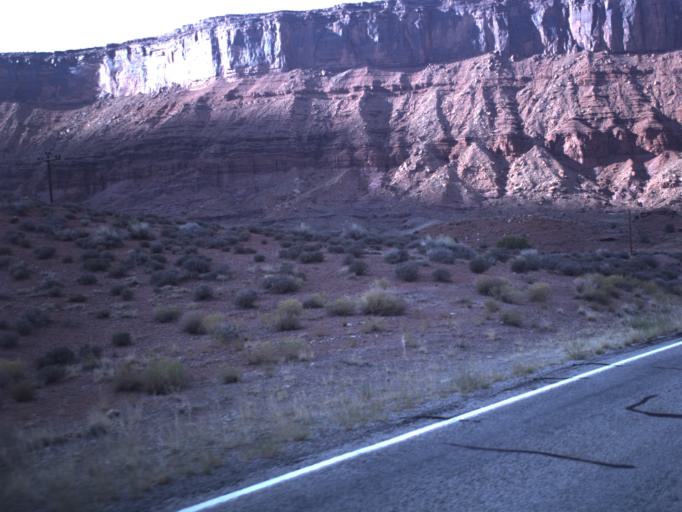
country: US
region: Utah
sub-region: Grand County
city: Moab
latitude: 38.7479
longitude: -109.3300
